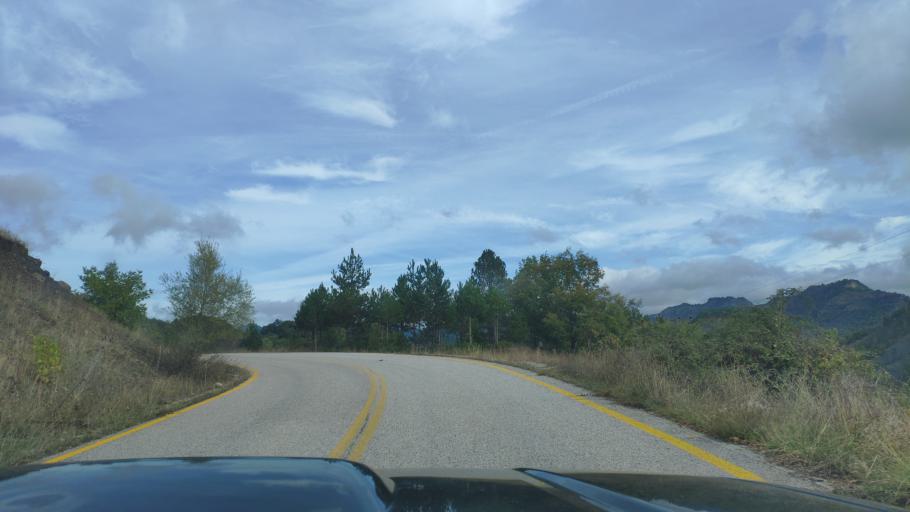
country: GR
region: West Macedonia
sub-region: Nomos Kastorias
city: Nestorio
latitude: 40.2446
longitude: 20.9892
